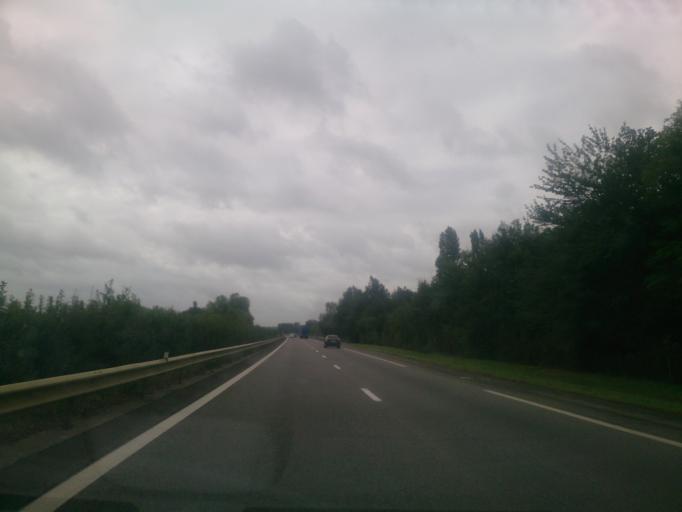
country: FR
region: Midi-Pyrenees
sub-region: Departement de la Haute-Garonne
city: Noe
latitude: 43.3678
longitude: 1.2741
